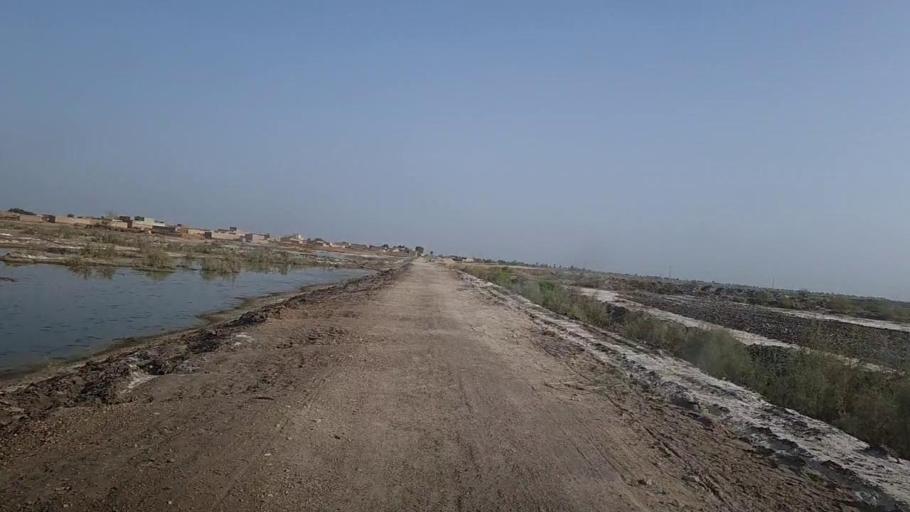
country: PK
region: Sindh
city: Sita Road
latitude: 27.1144
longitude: 67.8816
